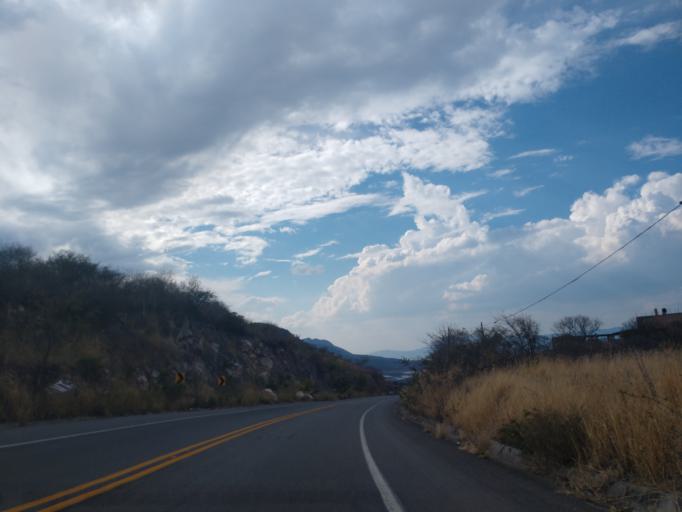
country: MX
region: Jalisco
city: Tizapan el Alto
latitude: 20.1250
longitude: -103.1584
